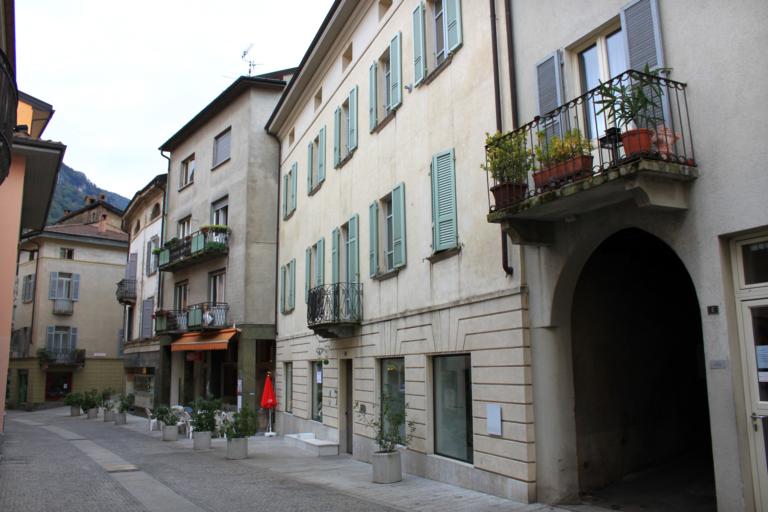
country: CH
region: Ticino
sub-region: Mendrisio District
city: Mendrisio
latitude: 45.8697
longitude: 8.9883
